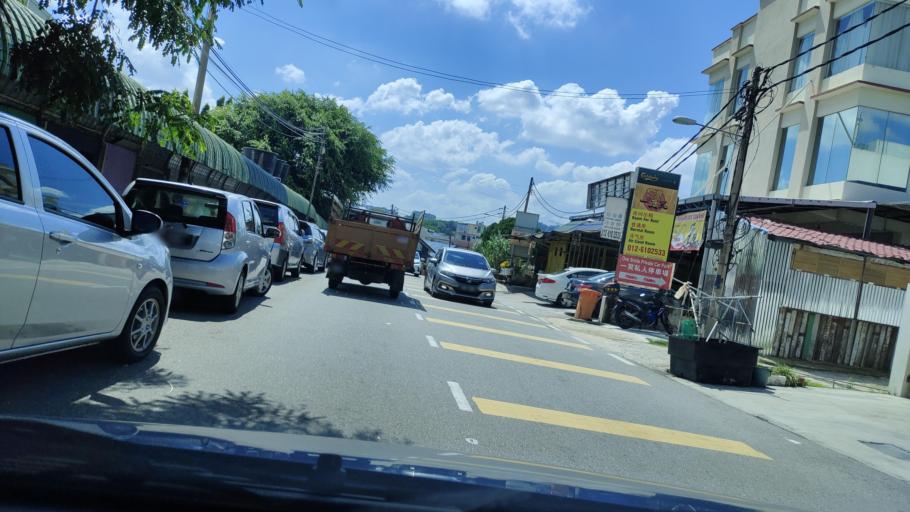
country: MY
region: Selangor
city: Kampong Baharu Balakong
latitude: 3.0259
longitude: 101.7009
